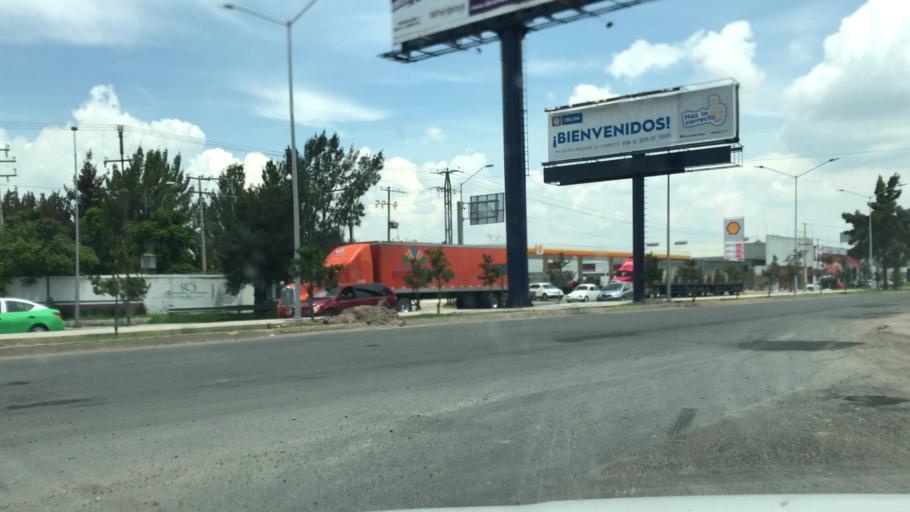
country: MX
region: Guanajuato
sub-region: Celaya
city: Roque
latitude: 20.5569
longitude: -100.8226
